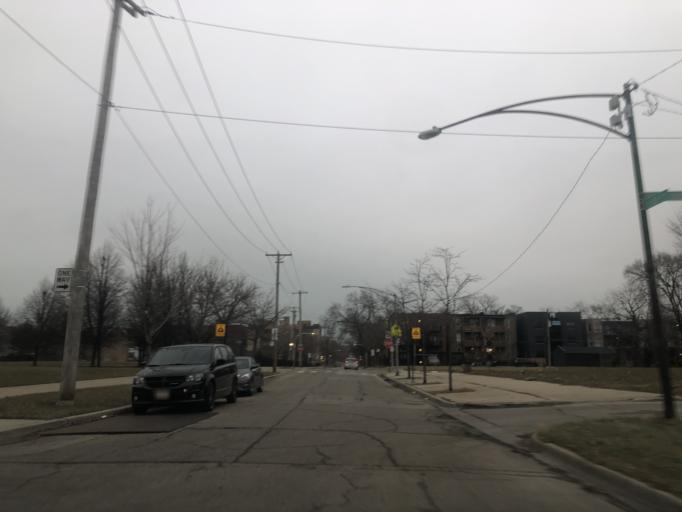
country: US
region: Illinois
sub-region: Cook County
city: Chicago
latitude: 41.7768
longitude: -87.5994
